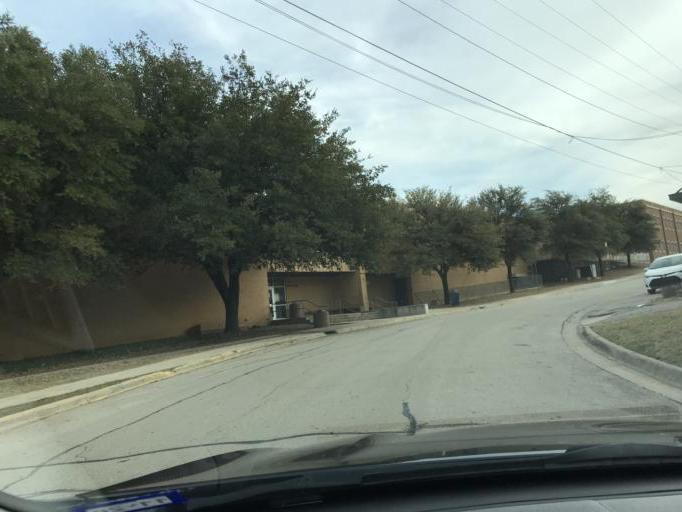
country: US
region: Texas
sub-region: Denton County
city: Denton
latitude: 33.2189
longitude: -97.1404
